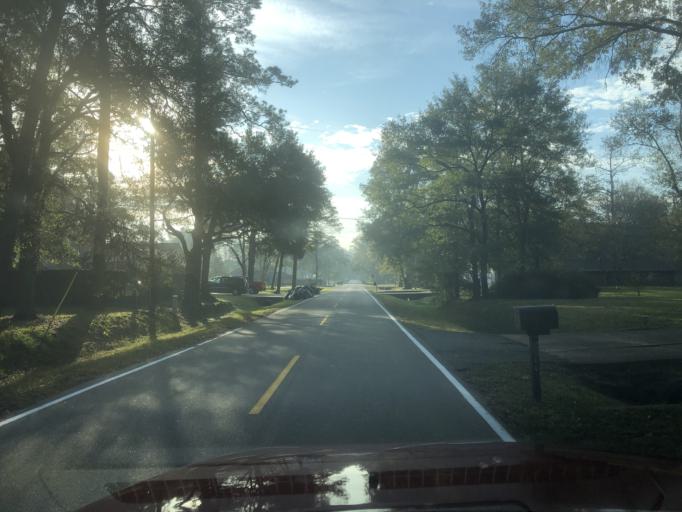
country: US
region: Texas
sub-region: Harris County
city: Spring
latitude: 30.0178
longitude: -95.4772
